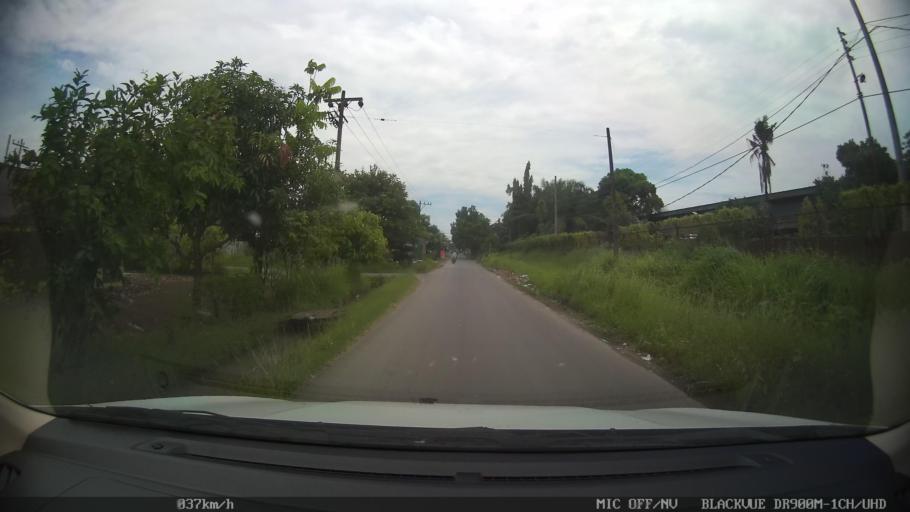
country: ID
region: North Sumatra
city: Sunggal
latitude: 3.6181
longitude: 98.5806
